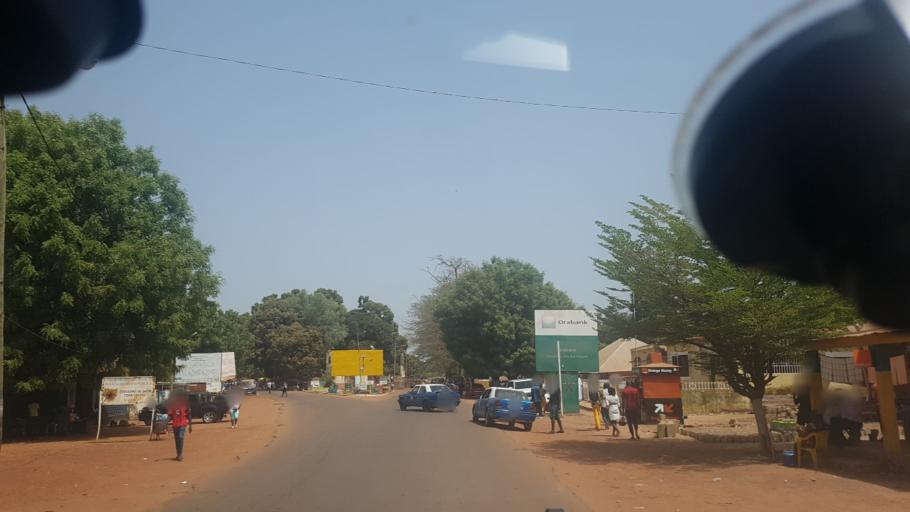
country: GW
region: Bissau
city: Bissau
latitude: 11.9548
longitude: -15.6489
